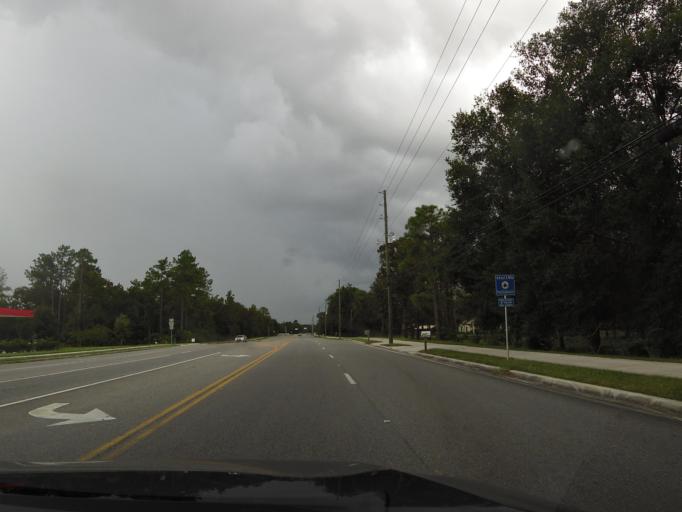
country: US
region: Florida
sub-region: Clay County
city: Asbury Lake
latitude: 30.0459
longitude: -81.8094
